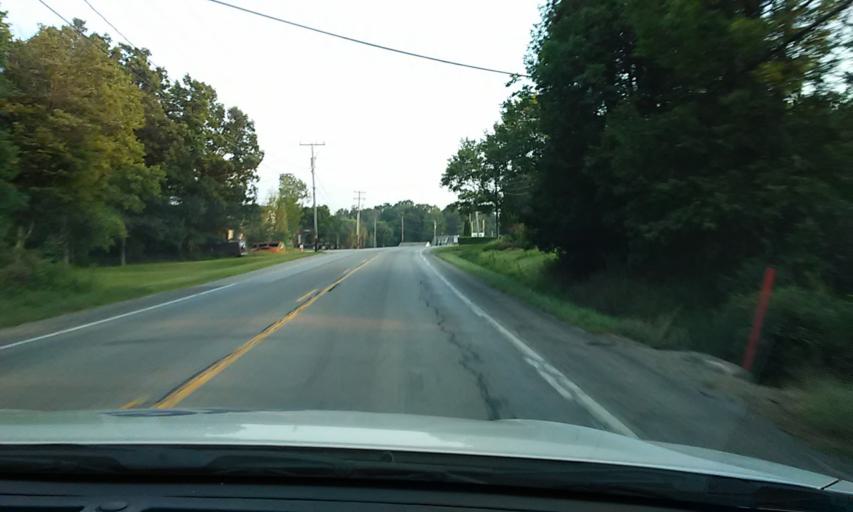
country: US
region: Pennsylvania
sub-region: Clarion County
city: Marianne
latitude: 41.3227
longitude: -79.3598
